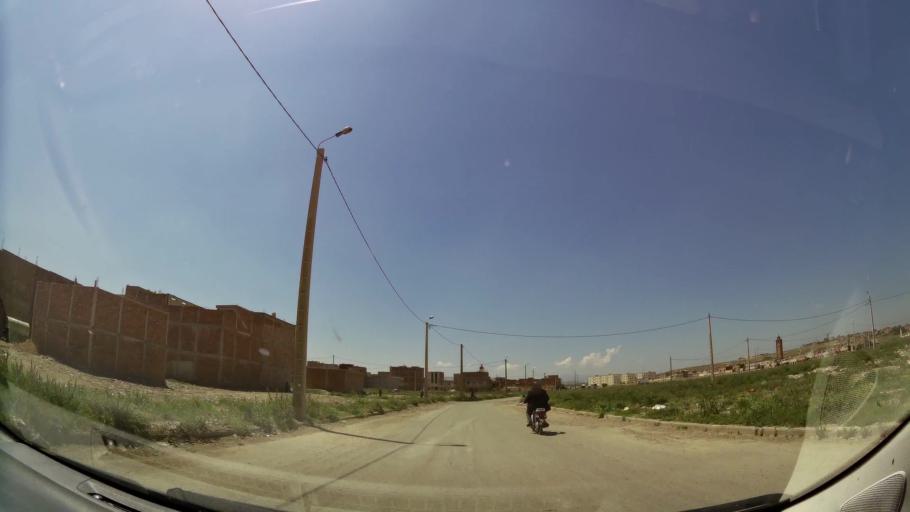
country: MA
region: Oriental
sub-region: Oujda-Angad
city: Oujda
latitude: 34.6915
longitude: -1.9358
